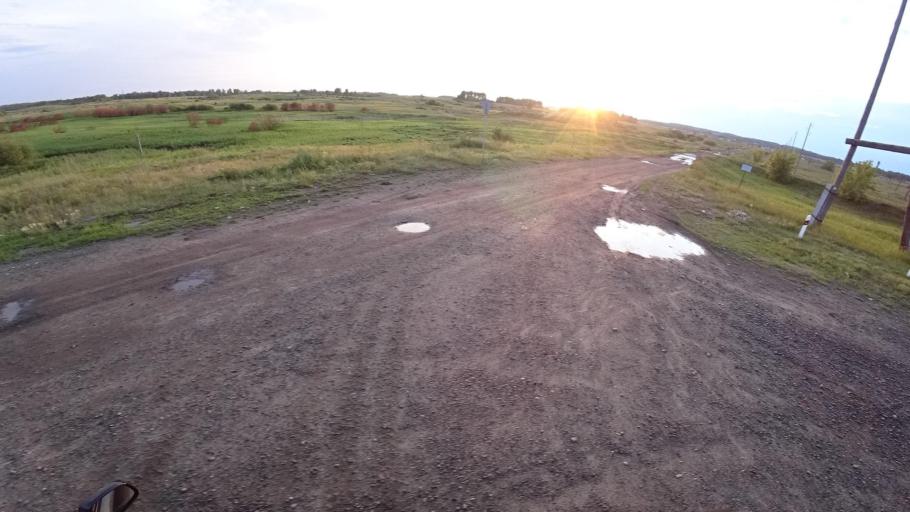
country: RU
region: Sverdlovsk
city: Kamyshlov
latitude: 56.8695
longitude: 62.7109
